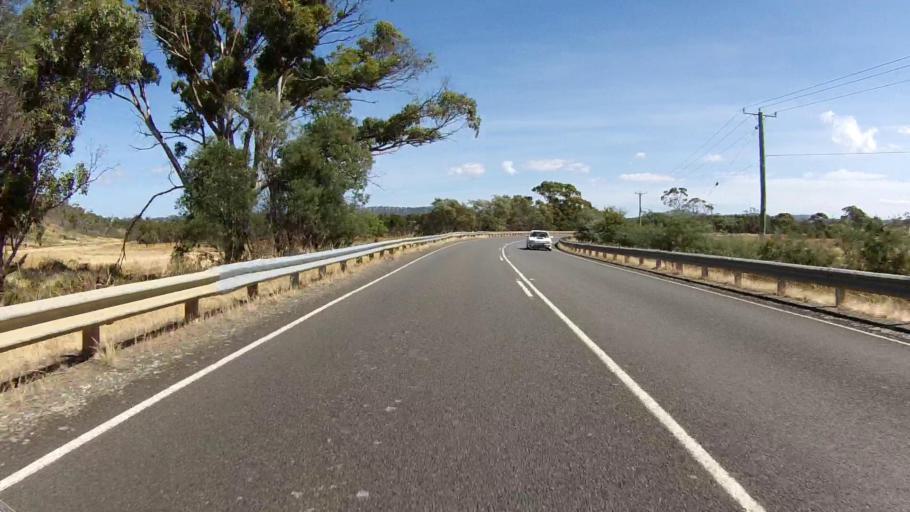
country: AU
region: Tasmania
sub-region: Sorell
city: Sorell
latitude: -42.5944
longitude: 147.7885
